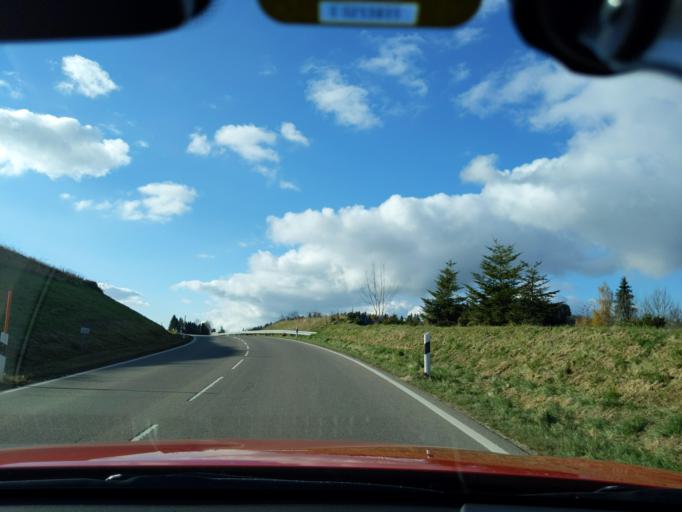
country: DE
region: Bavaria
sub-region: Swabia
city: Oberreute
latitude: 47.5671
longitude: 9.9496
